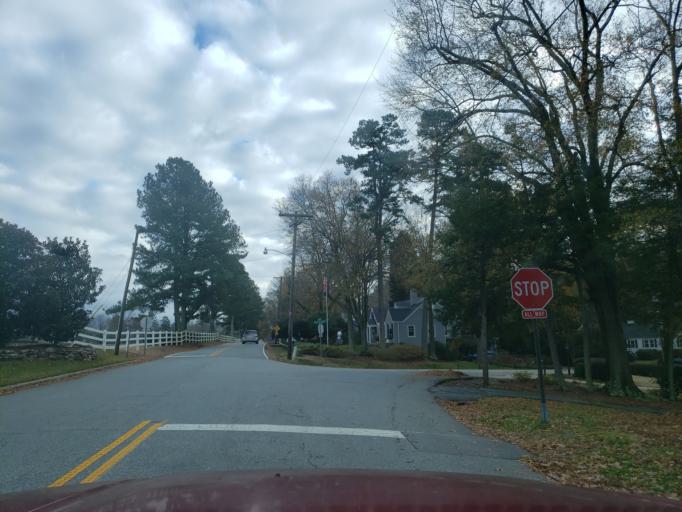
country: US
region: South Carolina
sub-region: Greenville County
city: Greenville
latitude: 34.8163
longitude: -82.3802
